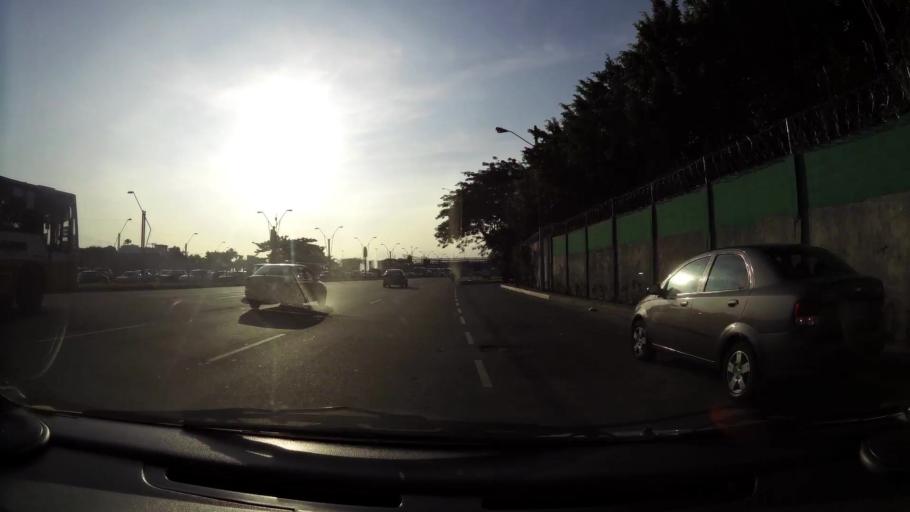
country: EC
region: Guayas
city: Eloy Alfaro
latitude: -2.1526
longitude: -79.8676
